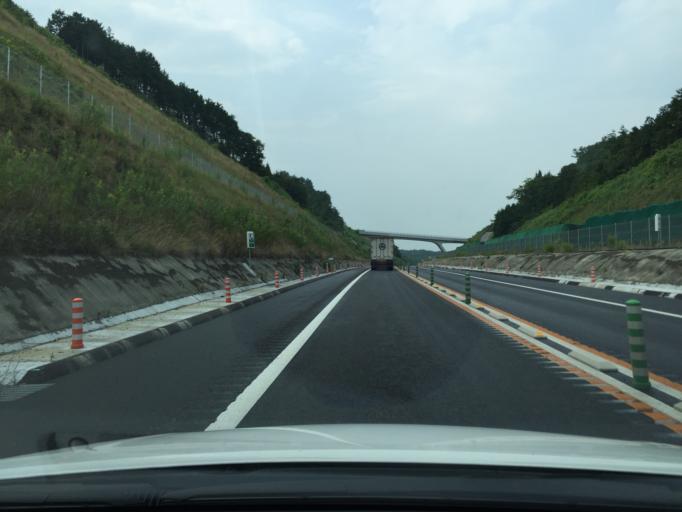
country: JP
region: Fukushima
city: Namie
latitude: 37.4384
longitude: 140.9581
